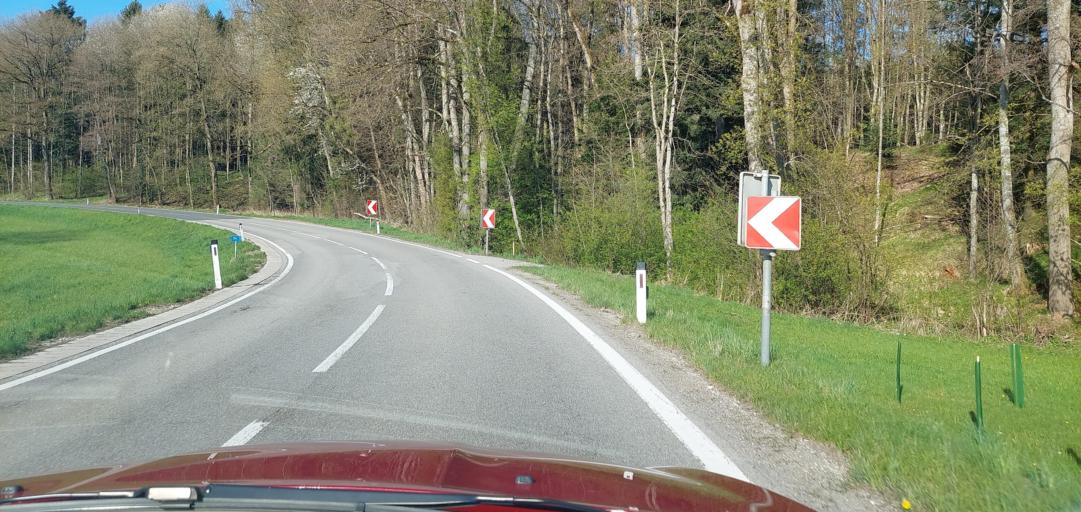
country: AT
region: Upper Austria
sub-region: Politischer Bezirk Ried im Innkreis
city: Ried im Innkreis
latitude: 48.1776
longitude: 13.5441
